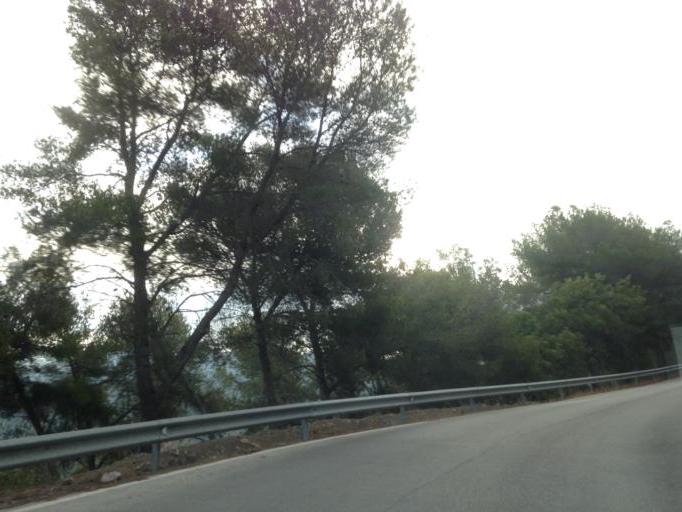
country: ES
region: Andalusia
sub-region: Provincia de Malaga
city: Malaga
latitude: 36.7675
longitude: -4.4041
